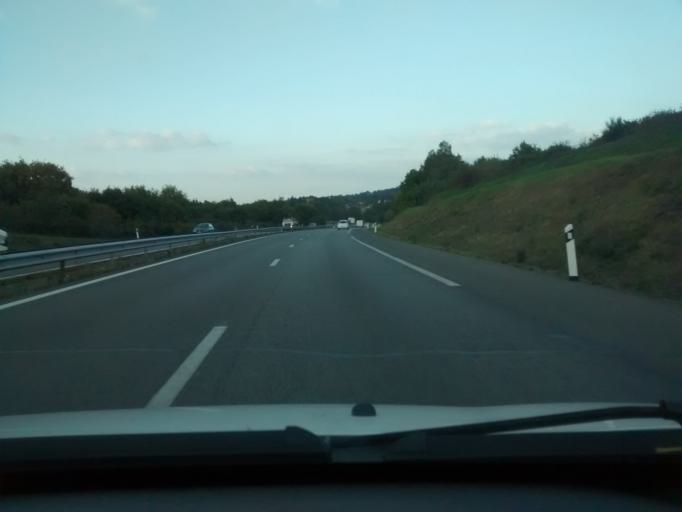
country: FR
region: Brittany
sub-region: Departement d'Ille-et-Vilaine
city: Bain-de-Bretagne
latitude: 47.8684
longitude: -1.6906
